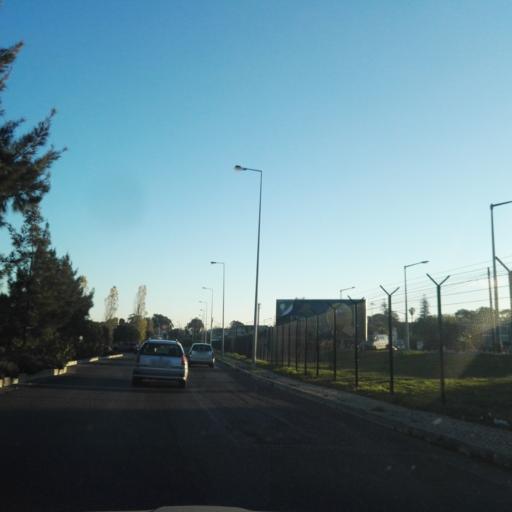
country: PT
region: Lisbon
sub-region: Loures
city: Sacavem
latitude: 38.7820
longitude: -9.1247
